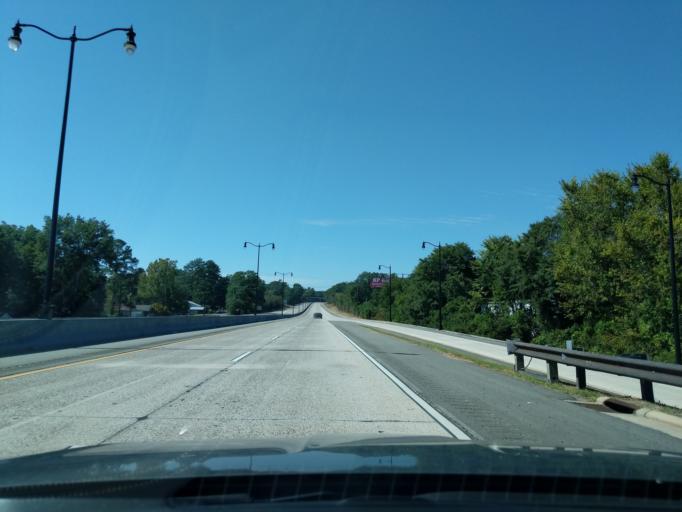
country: US
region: Georgia
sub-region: Richmond County
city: Augusta
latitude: 33.4841
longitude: -81.9981
